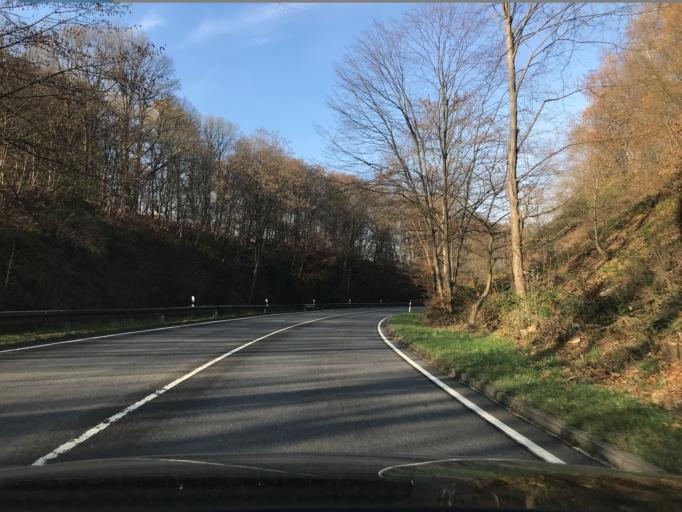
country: DE
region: North Rhine-Westphalia
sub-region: Regierungsbezirk Dusseldorf
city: Solingen
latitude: 51.1761
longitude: 7.1255
